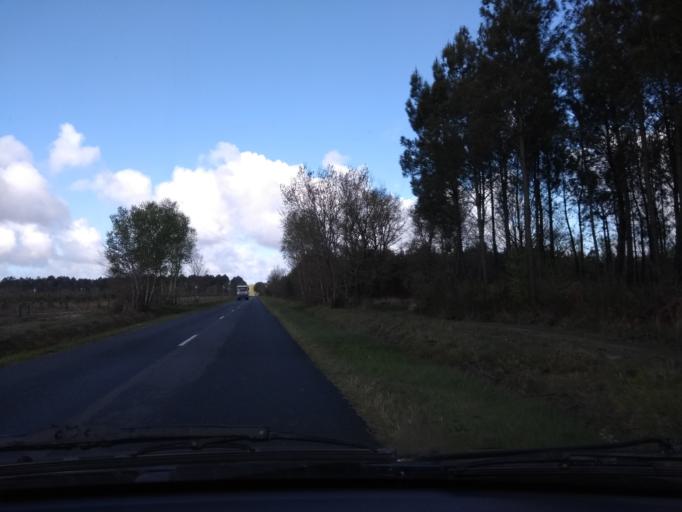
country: FR
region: Aquitaine
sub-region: Departement de la Gironde
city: Mios
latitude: 44.5501
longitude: -0.9727
